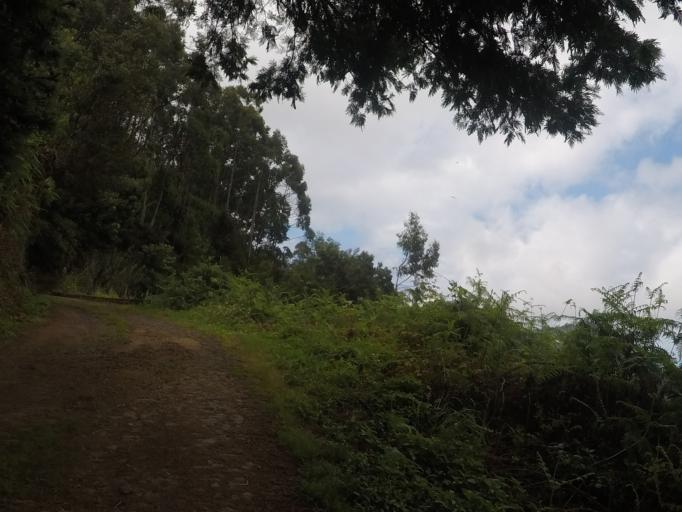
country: PT
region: Madeira
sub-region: Santana
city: Santana
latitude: 32.7752
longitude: -16.8776
